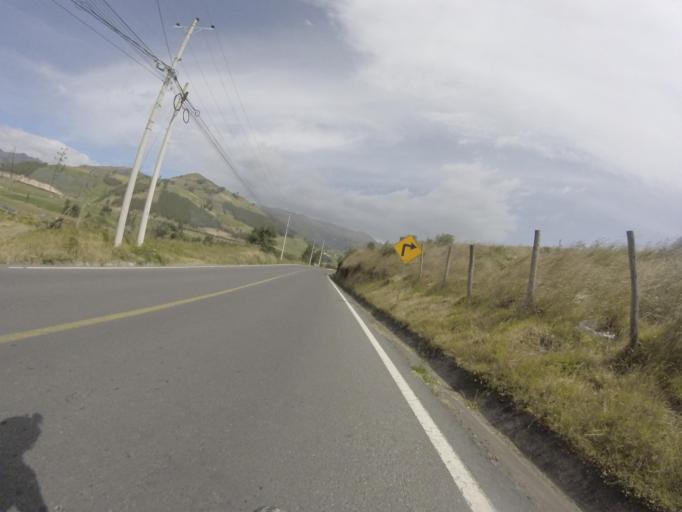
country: EC
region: Pichincha
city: Cayambe
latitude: 0.1243
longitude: -78.0830
